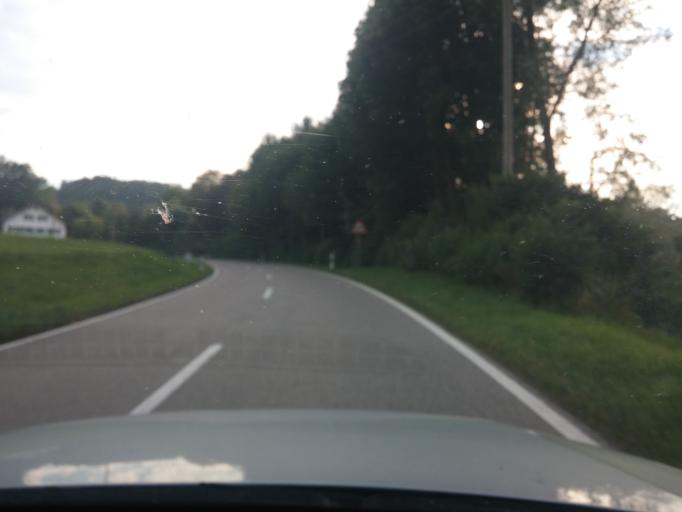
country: DE
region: Bavaria
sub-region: Swabia
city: Legau
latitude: 47.8499
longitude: 10.1828
